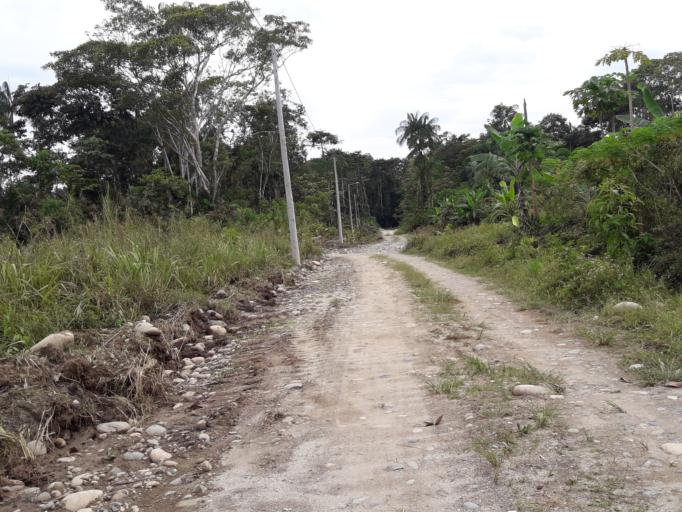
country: EC
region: Napo
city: Tena
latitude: -1.0561
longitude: -77.7927
